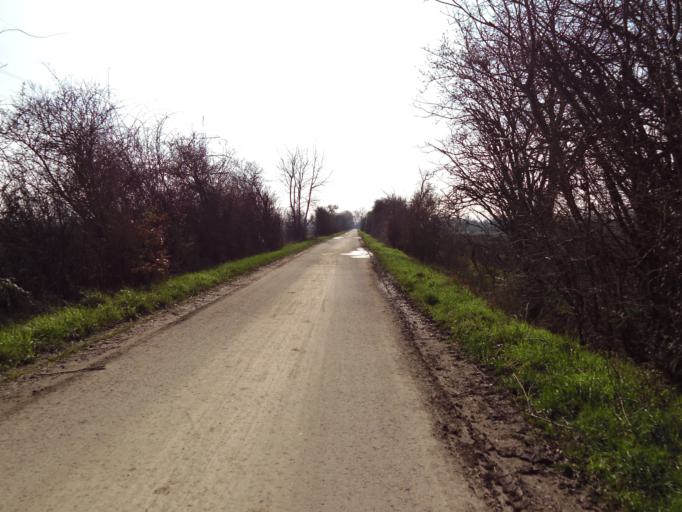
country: DE
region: Rheinland-Pfalz
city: Bobenheim-Roxheim
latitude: 49.5995
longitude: 8.4032
